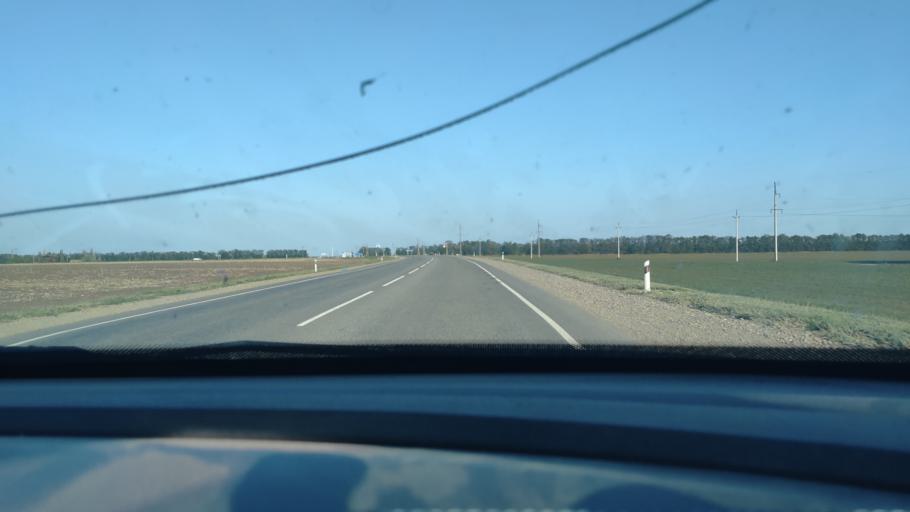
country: RU
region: Krasnodarskiy
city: Staroshcherbinovskaya
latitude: 46.6109
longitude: 38.6416
